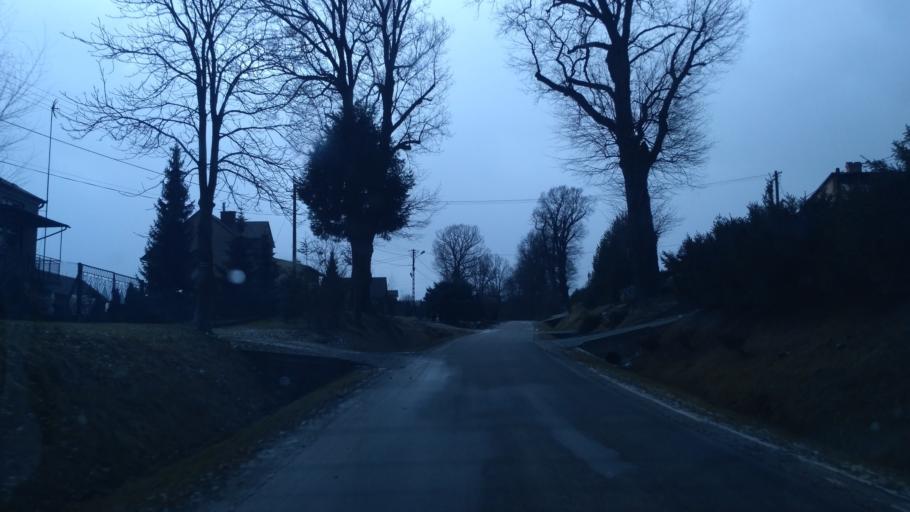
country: PL
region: Subcarpathian Voivodeship
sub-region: Powiat rzeszowski
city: Hyzne
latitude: 49.9051
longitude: 22.1968
